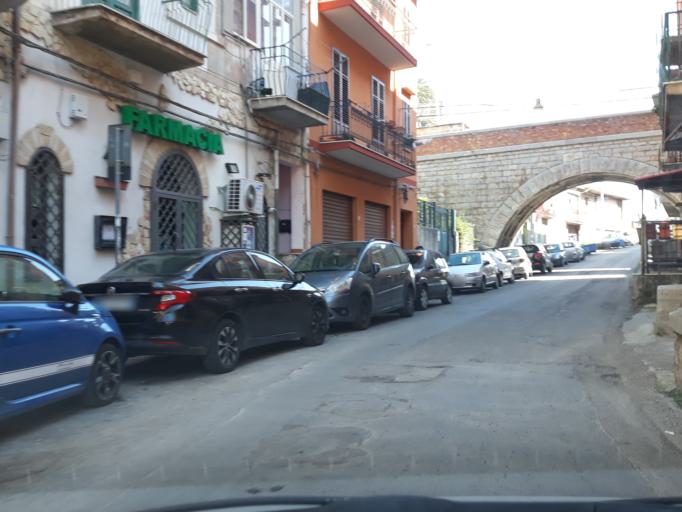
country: IT
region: Sicily
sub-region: Palermo
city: Piano dei Geli
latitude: 38.1085
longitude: 13.3059
